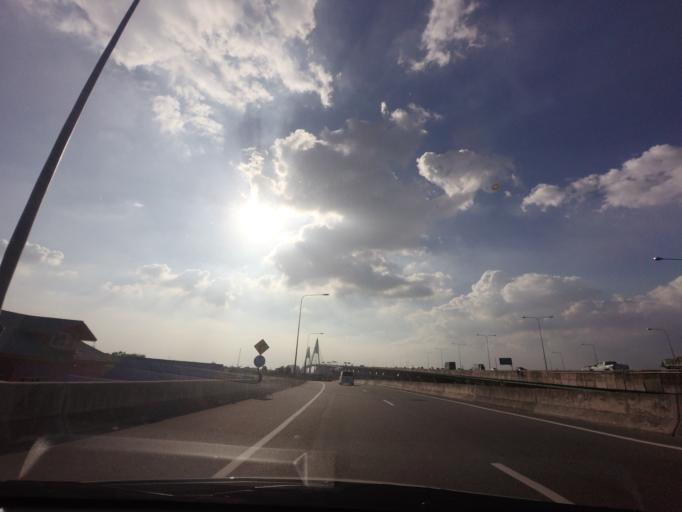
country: TH
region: Samut Prakan
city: Phra Pradaeng
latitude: 13.6385
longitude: 100.5534
